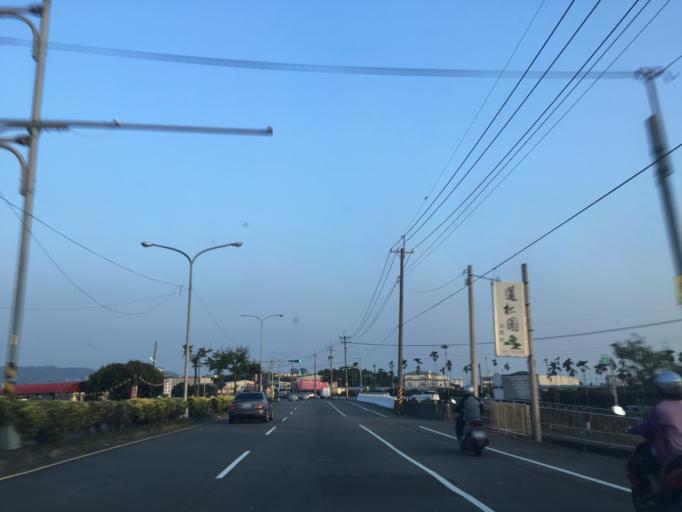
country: TW
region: Taiwan
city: Zhongxing New Village
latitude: 23.9935
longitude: 120.6662
